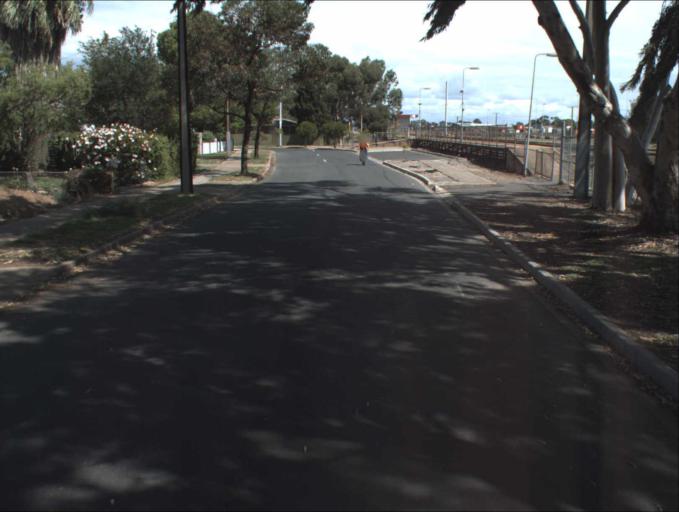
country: AU
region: South Australia
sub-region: Port Adelaide Enfield
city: Blair Athol
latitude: -34.8593
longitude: 138.5785
